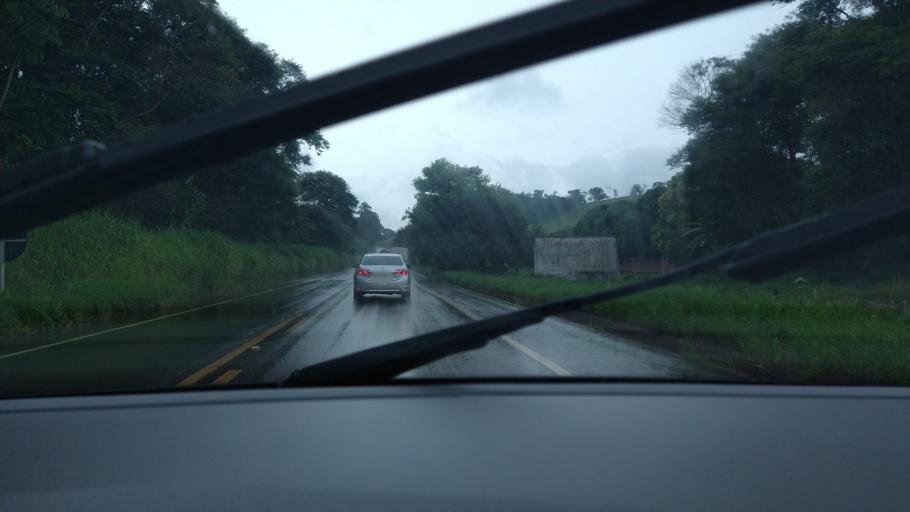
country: BR
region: Minas Gerais
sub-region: Vicosa
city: Vicosa
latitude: -20.6244
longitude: -42.8696
